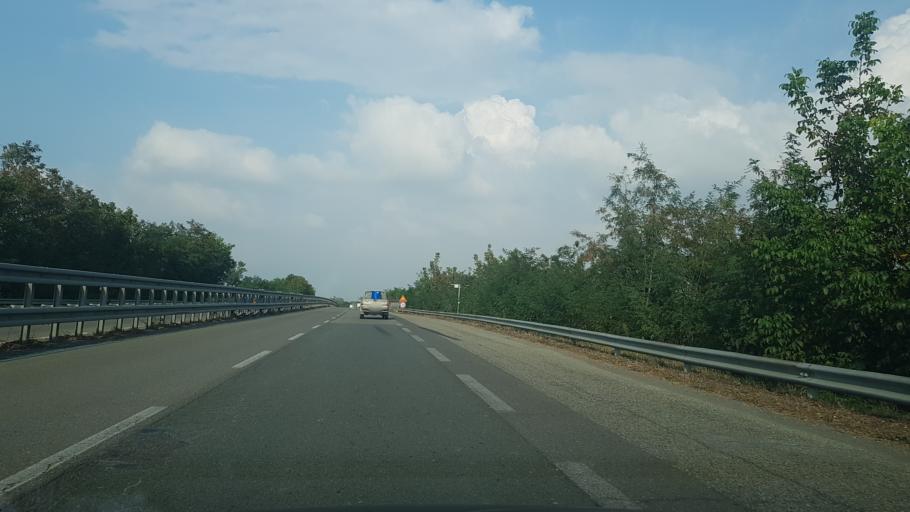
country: IT
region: Piedmont
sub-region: Provincia di Alessandria
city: Alessandria
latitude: 44.8914
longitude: 8.6241
